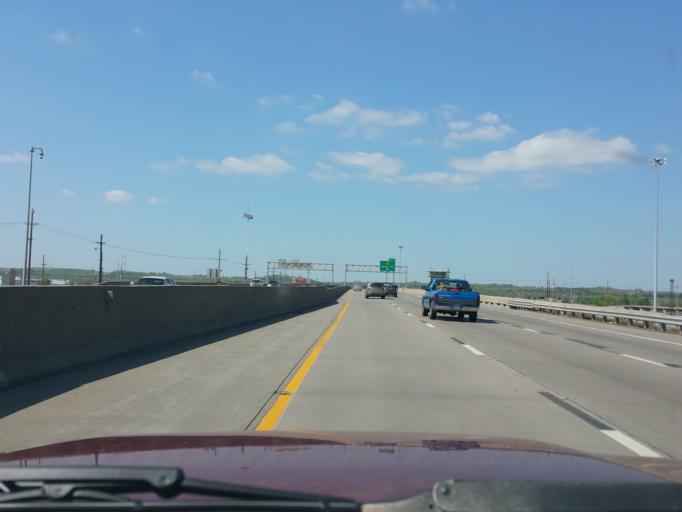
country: US
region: Kansas
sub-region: Johnson County
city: Shawnee
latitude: 39.0797
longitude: -94.6805
